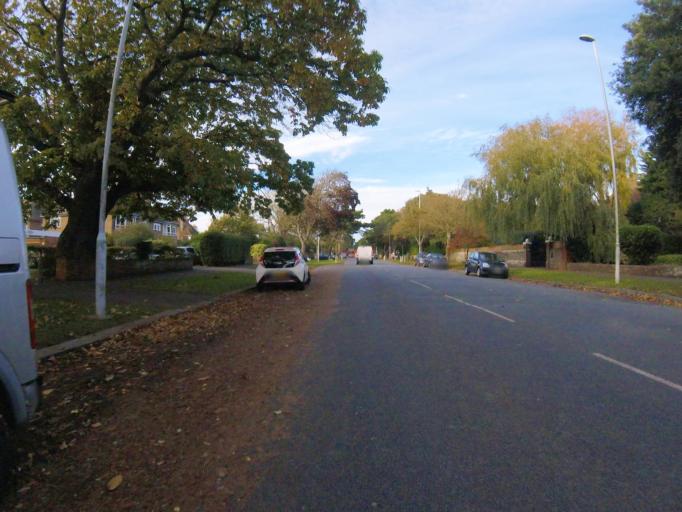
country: GB
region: England
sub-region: West Sussex
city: Worthing
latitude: 50.8124
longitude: -0.3933
